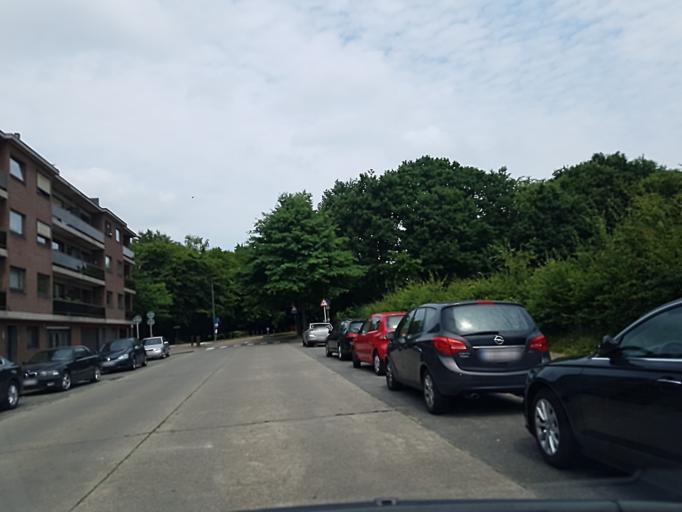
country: BE
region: Flanders
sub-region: Provincie Antwerpen
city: Schoten
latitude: 51.2316
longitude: 4.4834
